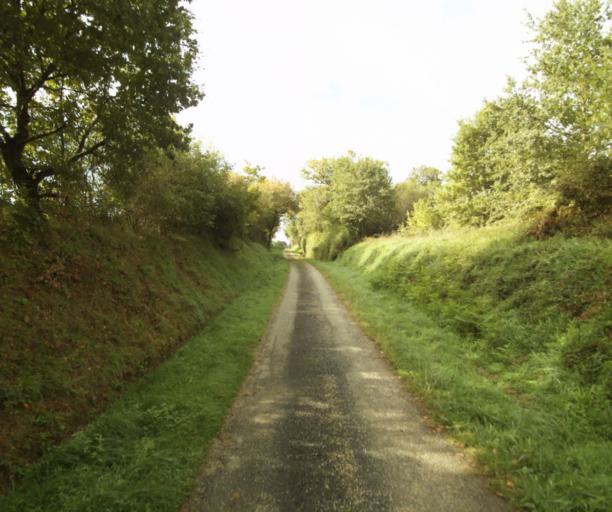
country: FR
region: Midi-Pyrenees
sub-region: Departement du Gers
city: Nogaro
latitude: 43.8240
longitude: -0.0744
